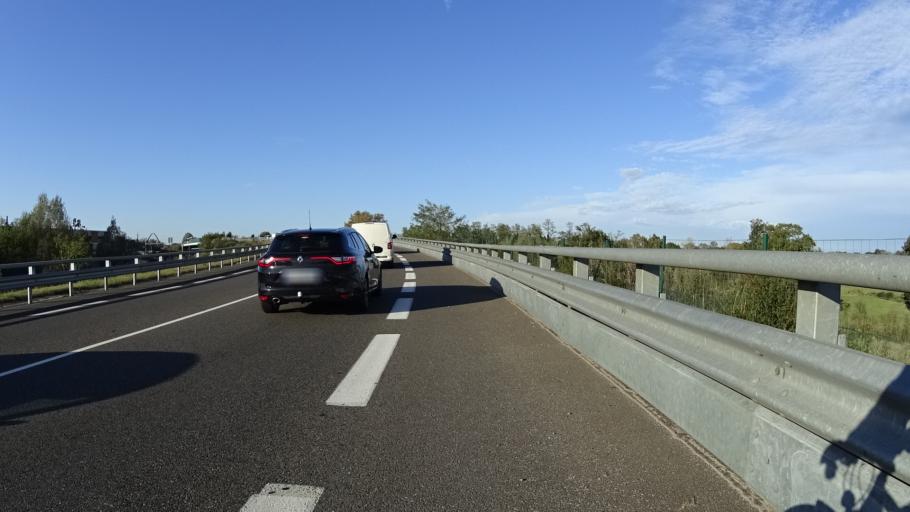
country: FR
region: Aquitaine
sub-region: Departement des Landes
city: Saint-Paul-les-Dax
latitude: 43.7260
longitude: -1.0357
